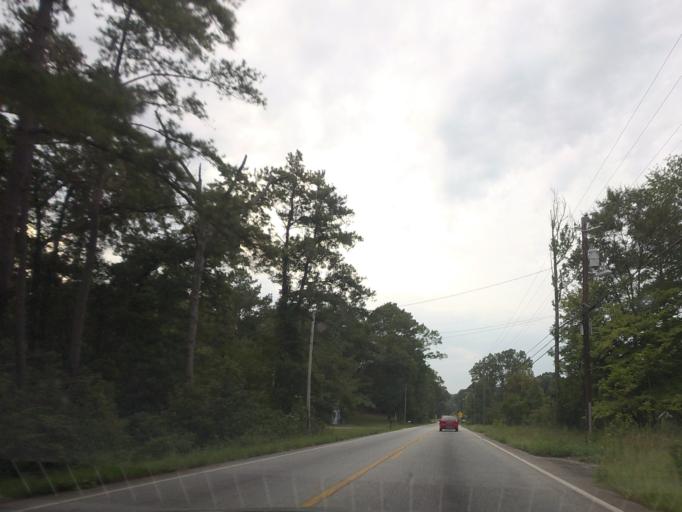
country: US
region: Georgia
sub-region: Bibb County
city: Macon
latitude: 32.8284
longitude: -83.5352
